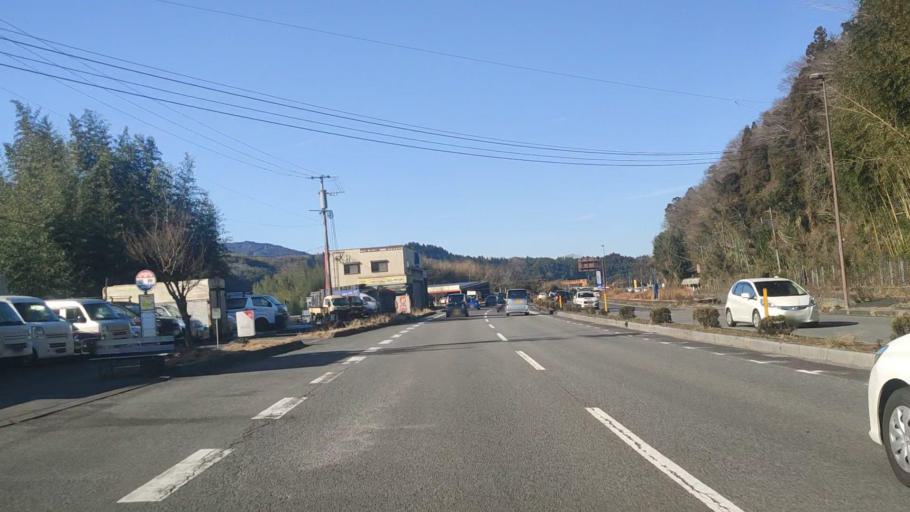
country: JP
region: Oita
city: Oita
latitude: 33.1141
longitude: 131.6550
